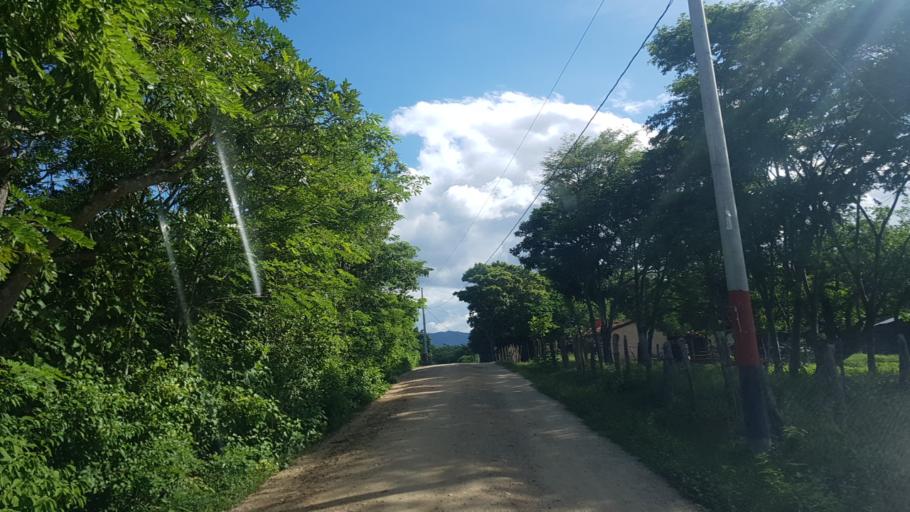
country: NI
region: Nueva Segovia
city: Mozonte
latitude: 13.6479
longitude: -86.3985
